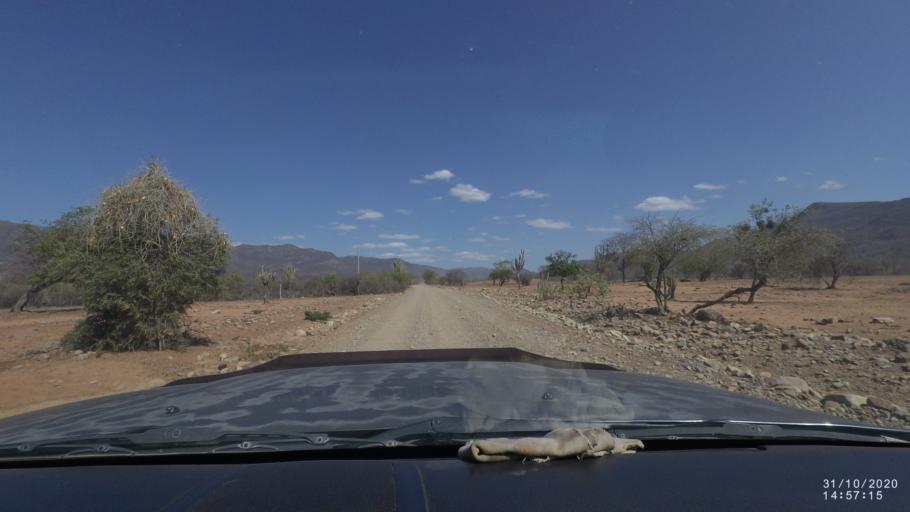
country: BO
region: Cochabamba
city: Aiquile
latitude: -18.2423
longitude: -64.8449
